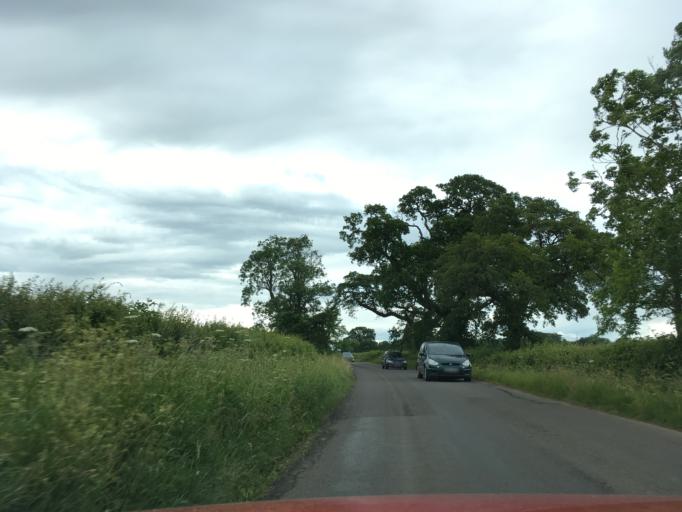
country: GB
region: England
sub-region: Wiltshire
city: Norton
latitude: 51.5951
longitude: -2.1803
